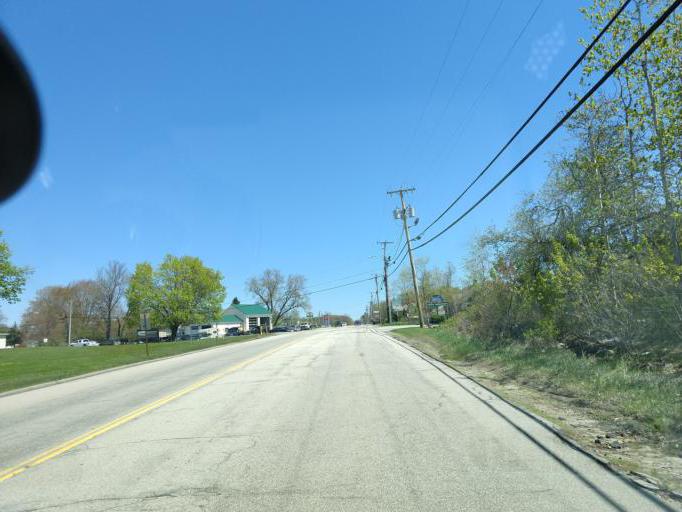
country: US
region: Maine
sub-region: York County
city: Kittery
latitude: 43.1197
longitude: -70.7223
